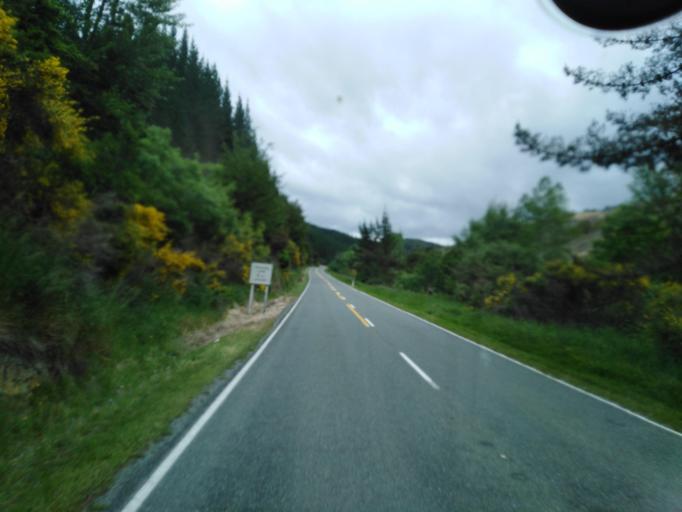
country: NZ
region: Tasman
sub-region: Tasman District
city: Wakefield
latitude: -41.6229
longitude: 172.7445
